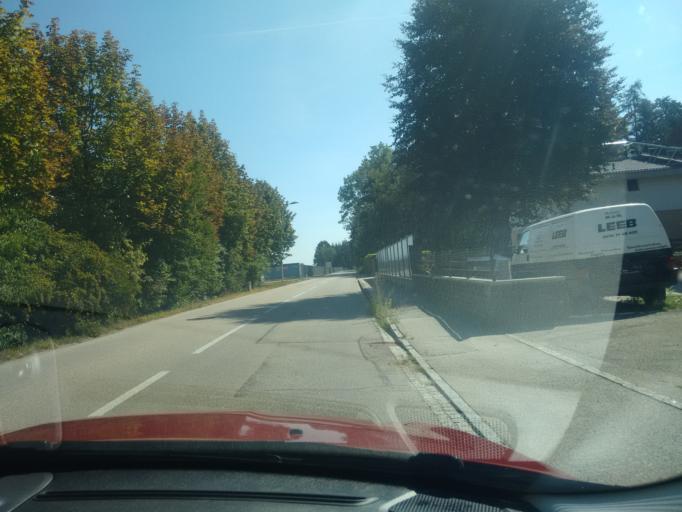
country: AT
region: Upper Austria
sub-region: Wels-Land
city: Steinhaus
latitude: 48.1190
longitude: 14.0300
